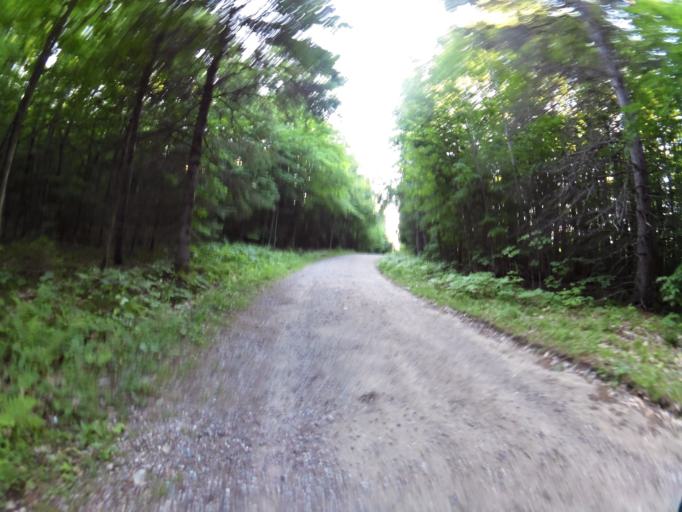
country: CA
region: Quebec
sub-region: Outaouais
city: Wakefield
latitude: 45.5955
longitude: -75.9927
